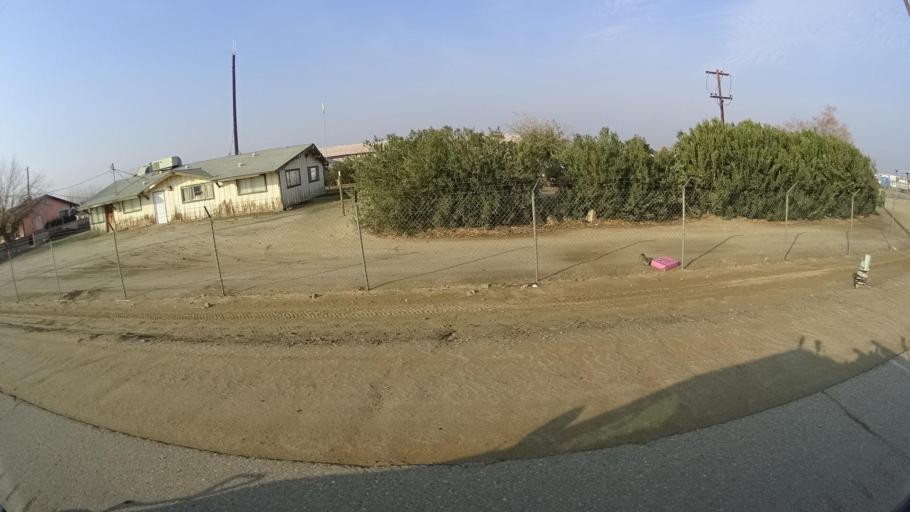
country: US
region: California
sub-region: Kern County
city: Weedpatch
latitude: 35.1447
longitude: -118.9146
